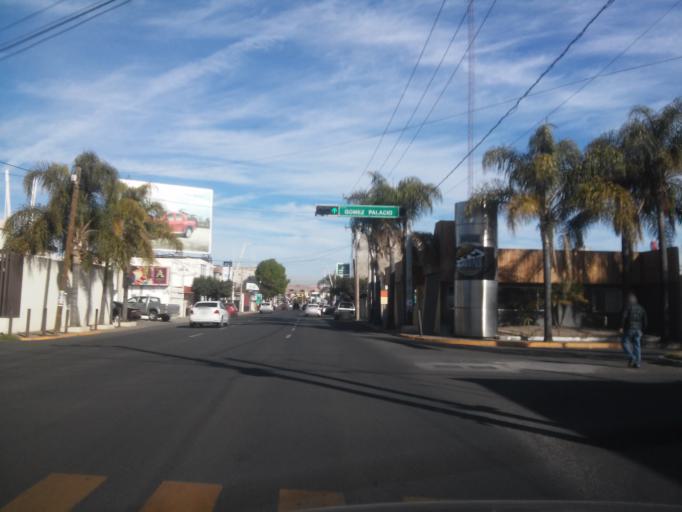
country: MX
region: Durango
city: Victoria de Durango
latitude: 24.0333
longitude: -104.6538
